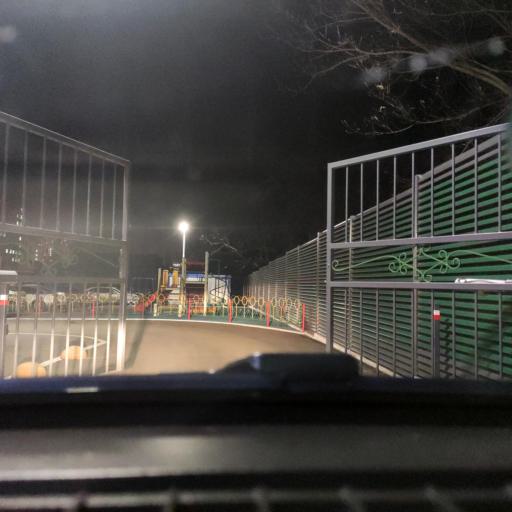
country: RU
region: Voronezj
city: Voronezh
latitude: 51.7023
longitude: 39.1801
